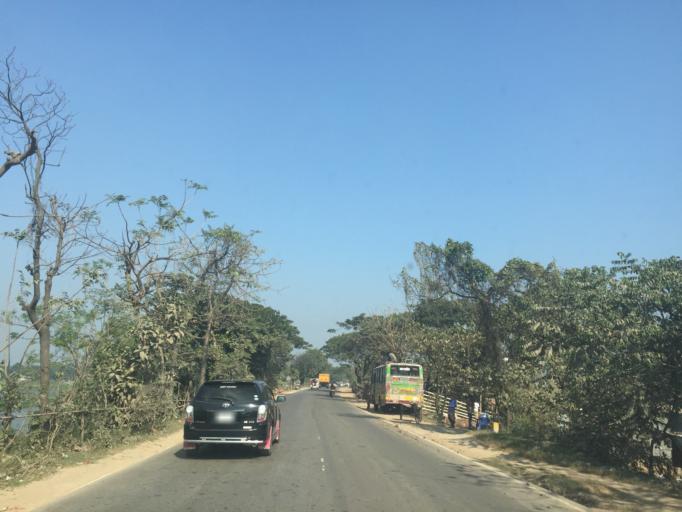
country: BD
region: Dhaka
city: Azimpur
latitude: 23.8134
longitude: 90.3404
